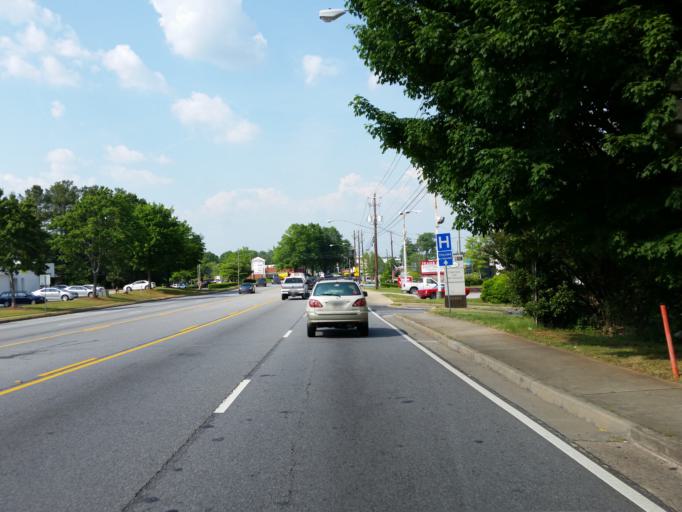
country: US
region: Georgia
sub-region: Fulton County
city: Roswell
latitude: 34.0472
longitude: -84.3394
